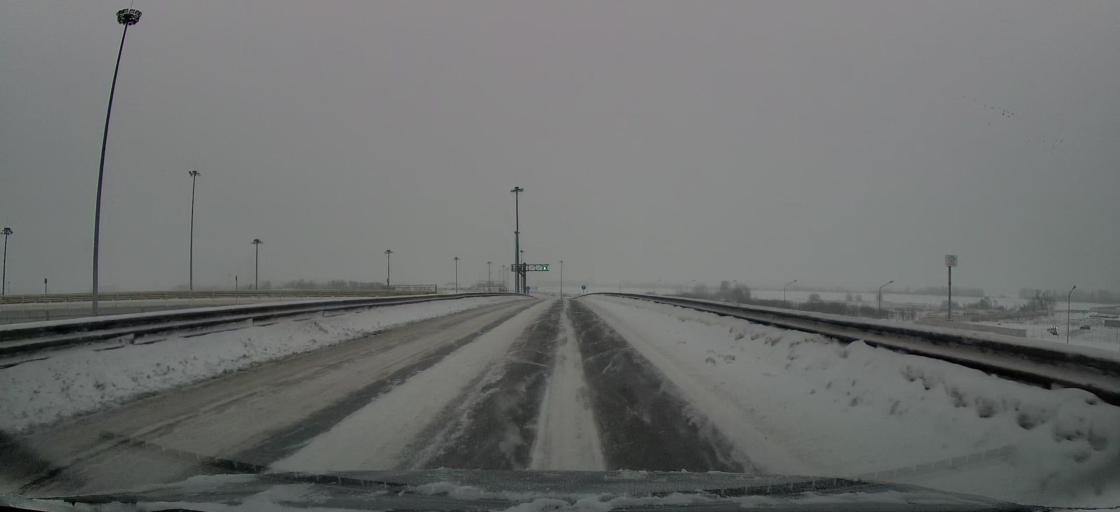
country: RU
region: St.-Petersburg
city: Sosnovaya Polyana
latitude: 59.7990
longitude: 30.1641
